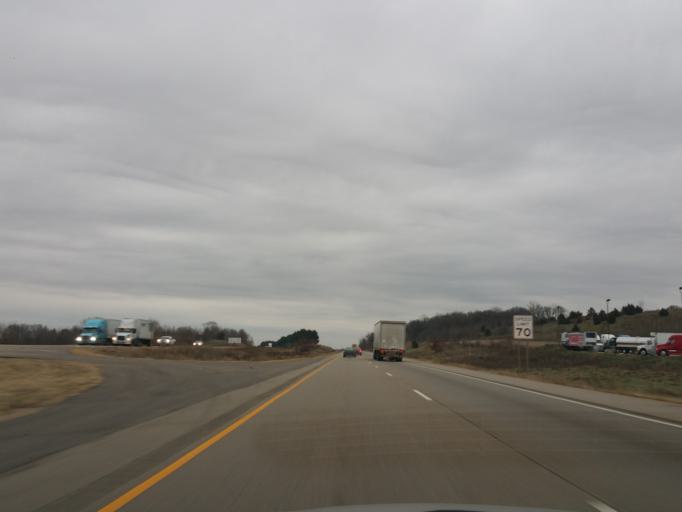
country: US
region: Wisconsin
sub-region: Saint Croix County
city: Roberts
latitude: 44.9537
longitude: -92.5492
